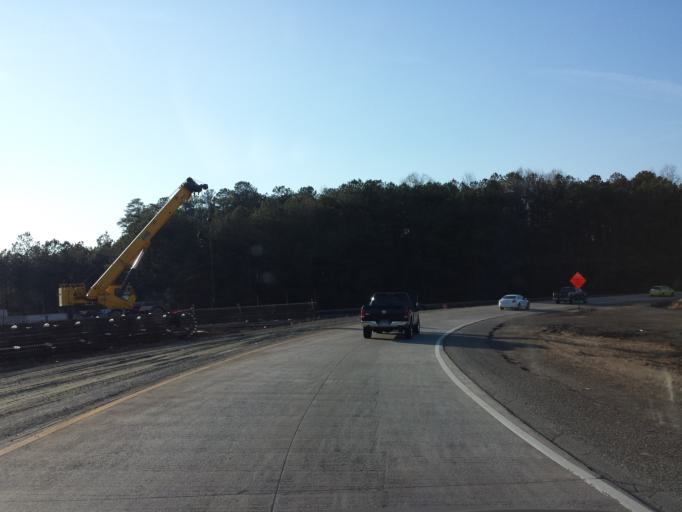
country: US
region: Georgia
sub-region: Cobb County
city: Marietta
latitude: 33.9838
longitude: -84.5438
